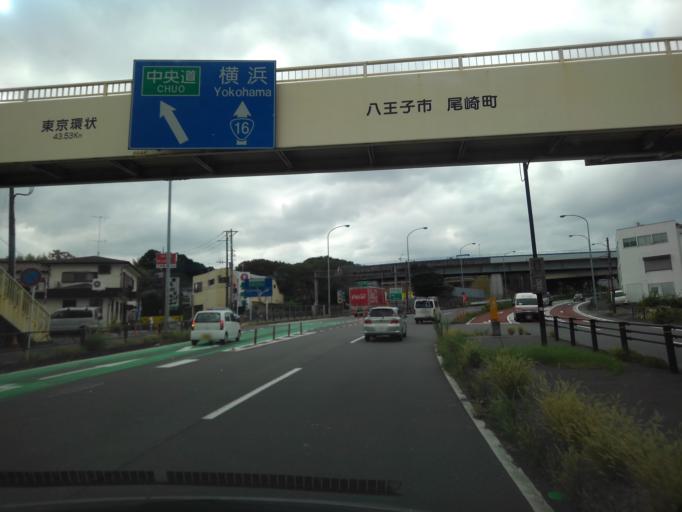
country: JP
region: Tokyo
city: Hachioji
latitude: 35.6807
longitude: 139.3434
